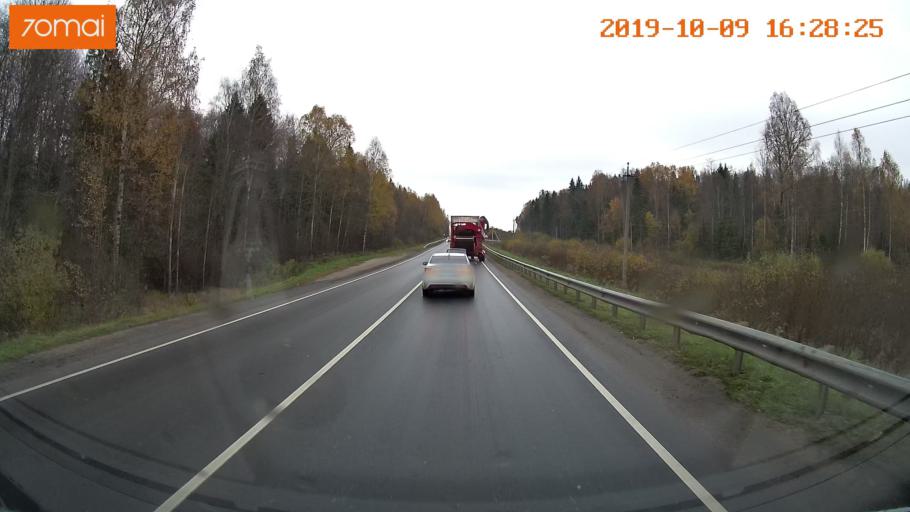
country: RU
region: Kostroma
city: Oktyabr'skiy
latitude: 57.6288
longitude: 40.9319
